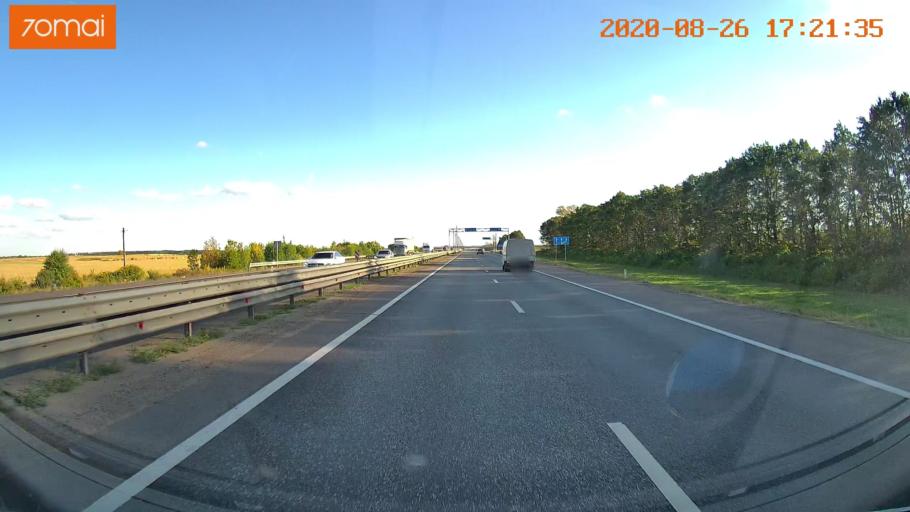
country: RU
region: Tula
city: Volovo
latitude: 53.5627
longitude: 38.1120
